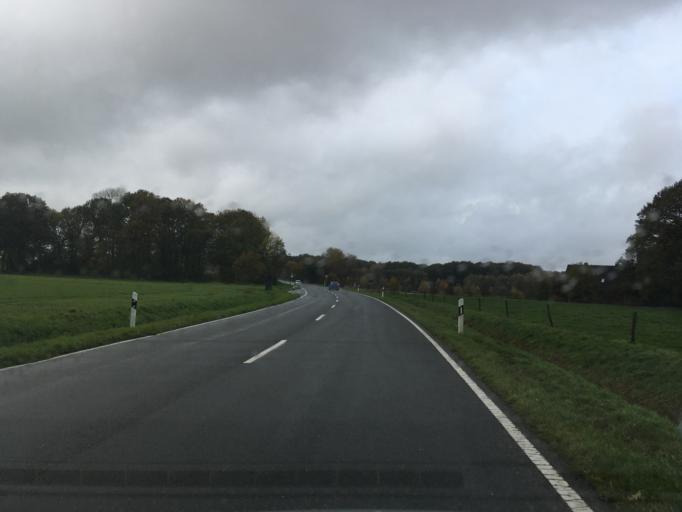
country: DE
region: North Rhine-Westphalia
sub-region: Regierungsbezirk Munster
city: Velen
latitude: 51.8738
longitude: 7.0175
